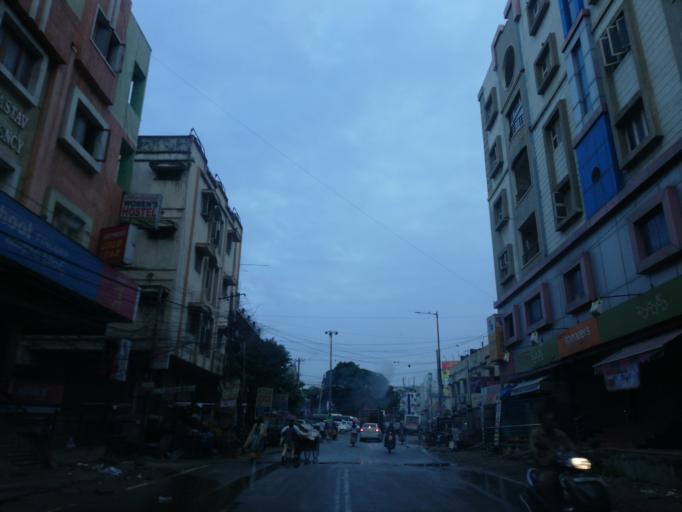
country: IN
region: Telangana
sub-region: Rangareddi
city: Kukatpalli
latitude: 17.4870
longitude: 78.3950
